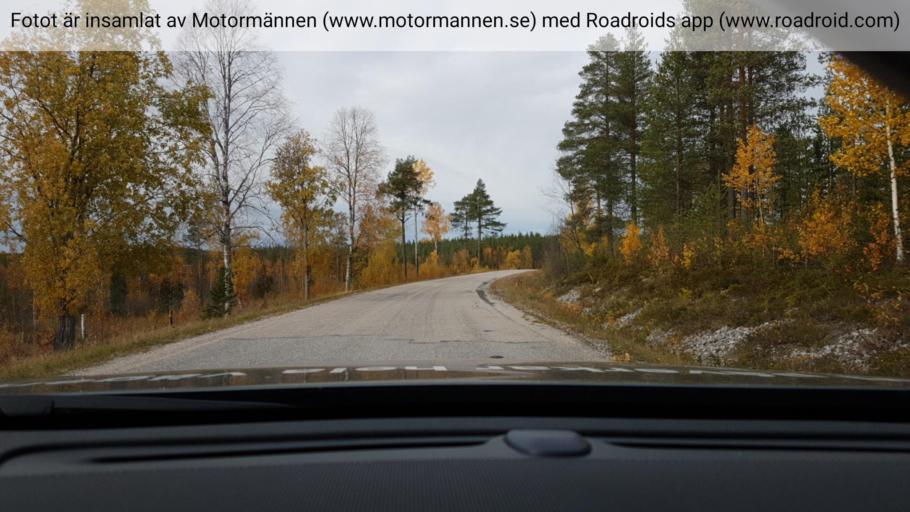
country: SE
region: Norrbotten
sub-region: Overkalix Kommun
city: OEverkalix
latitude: 66.2567
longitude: 23.1149
